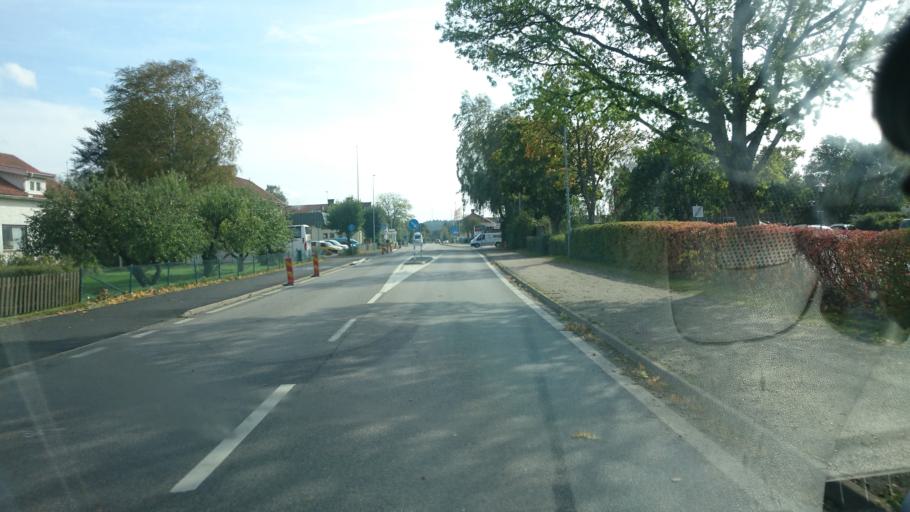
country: SE
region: Vaestra Goetaland
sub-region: Alingsas Kommun
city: Sollebrunn
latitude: 58.1211
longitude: 12.5296
